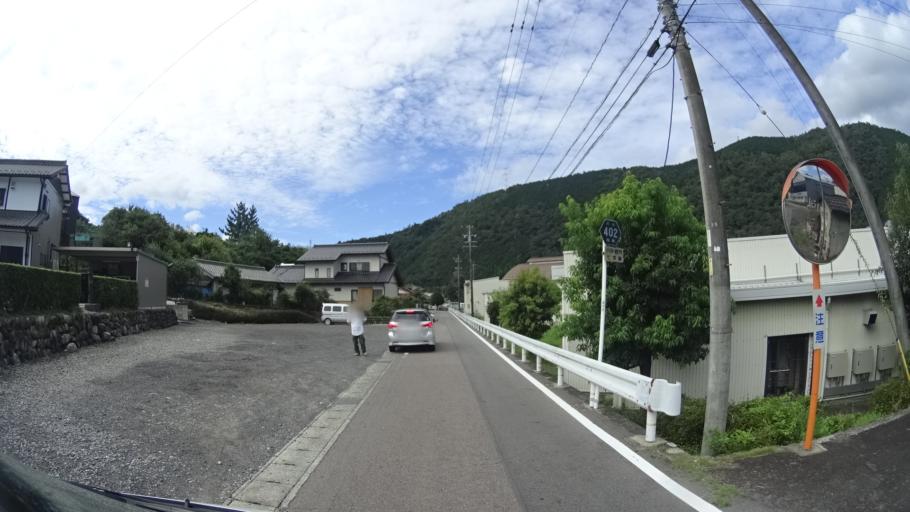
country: JP
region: Gifu
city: Minokamo
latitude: 35.5375
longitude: 137.1179
